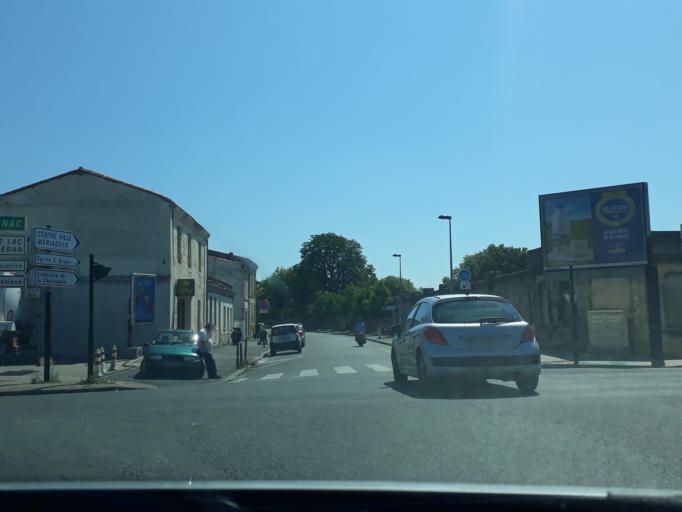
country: FR
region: Aquitaine
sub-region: Departement de la Gironde
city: Bordeaux
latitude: 44.8366
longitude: -0.5990
